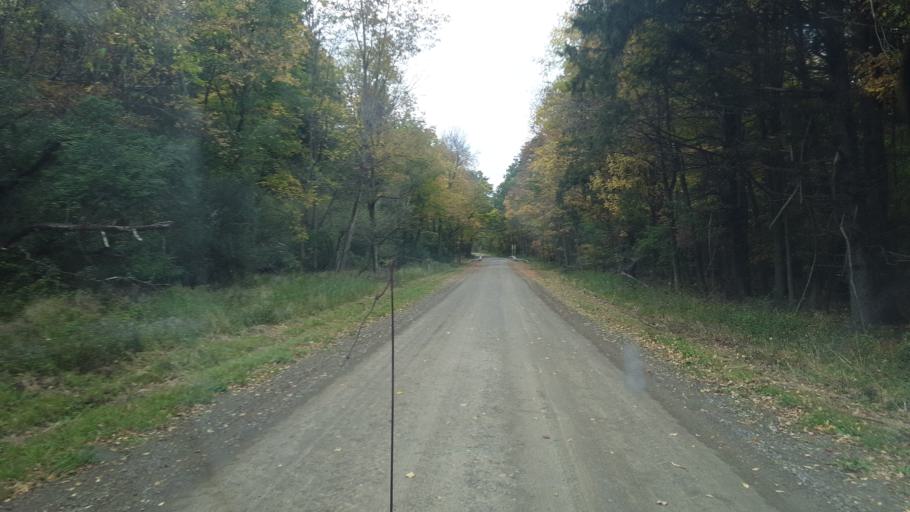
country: US
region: New York
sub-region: Allegany County
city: Alfred
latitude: 42.3715
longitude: -77.8491
